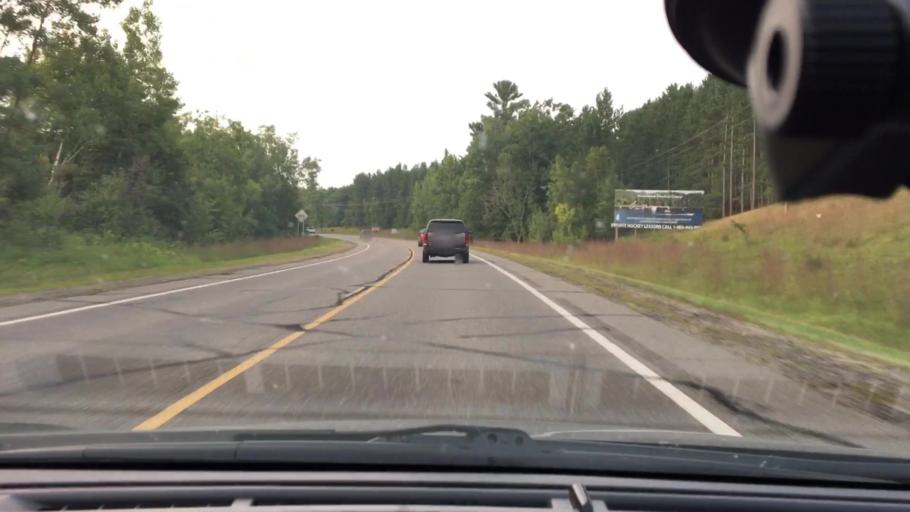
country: US
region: Minnesota
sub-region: Crow Wing County
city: Crosby
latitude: 46.4522
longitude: -93.8795
